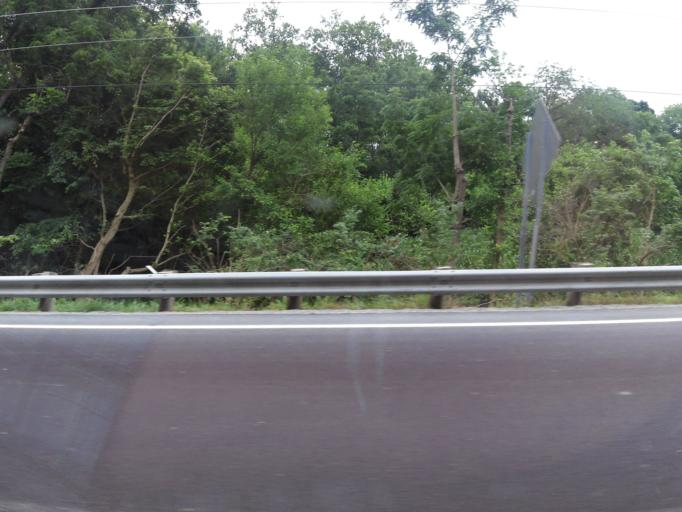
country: US
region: Ohio
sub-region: Clinton County
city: Blanchester
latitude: 39.2254
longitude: -83.9107
